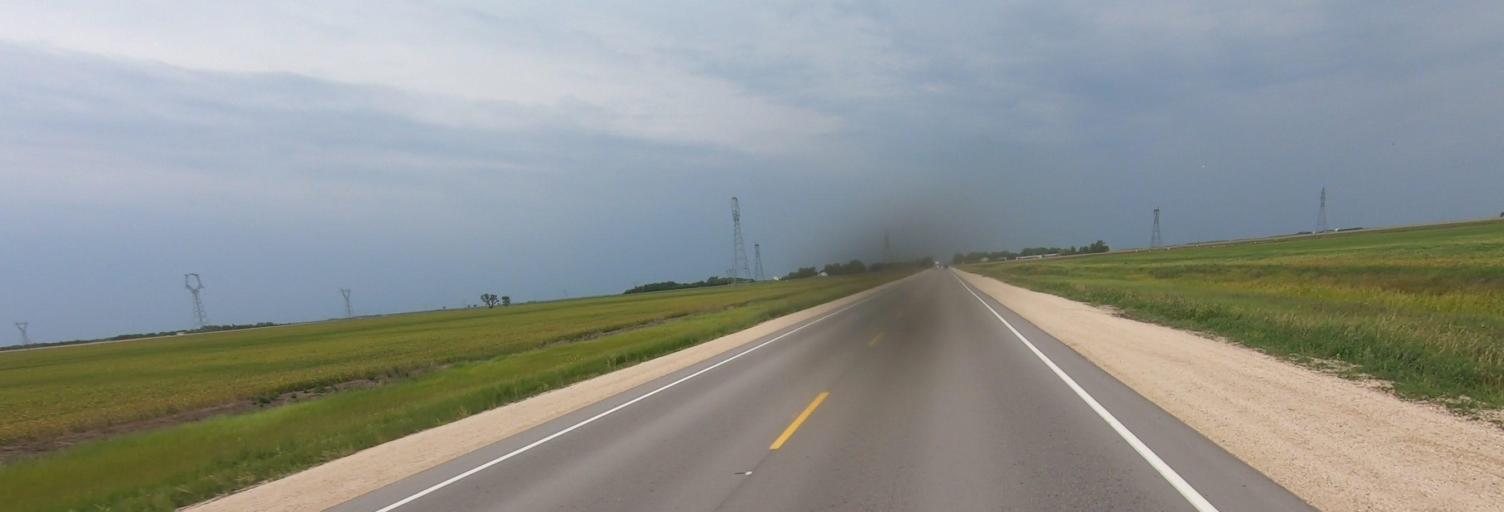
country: CA
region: Manitoba
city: Headingley
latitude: 49.7684
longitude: -97.3481
